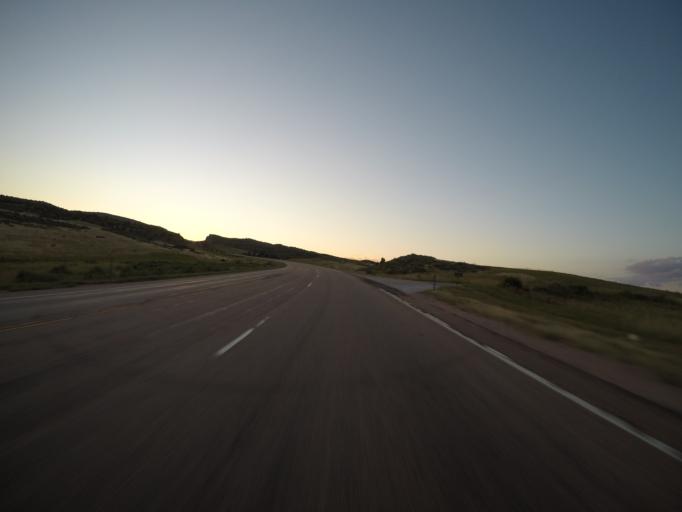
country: US
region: Colorado
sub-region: Larimer County
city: Laporte
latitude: 40.7583
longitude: -105.1719
